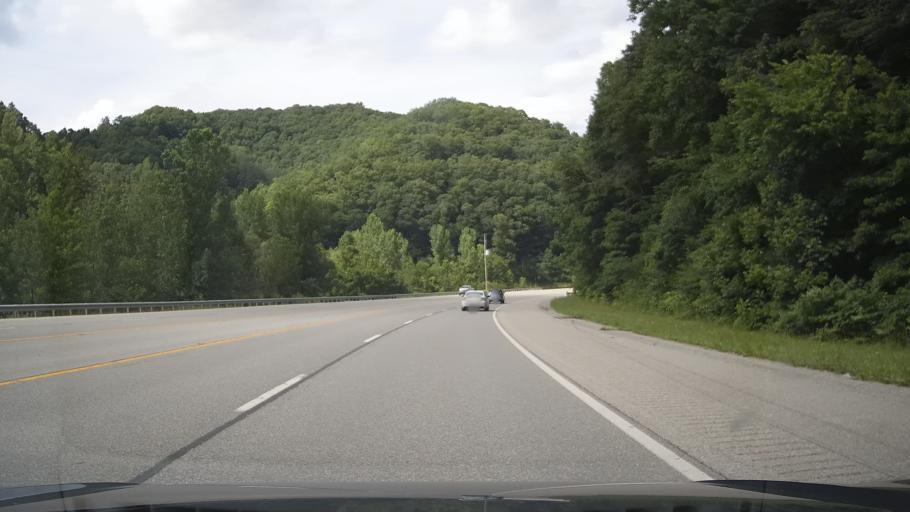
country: US
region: Kentucky
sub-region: Letcher County
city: Jenkins
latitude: 37.2476
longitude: -82.6207
